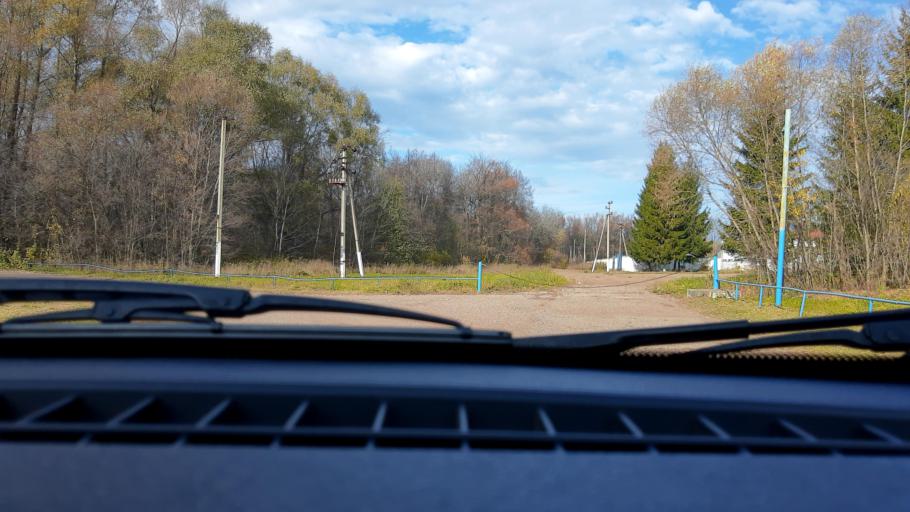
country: RU
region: Bashkortostan
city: Mikhaylovka
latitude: 54.8055
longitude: 55.8307
